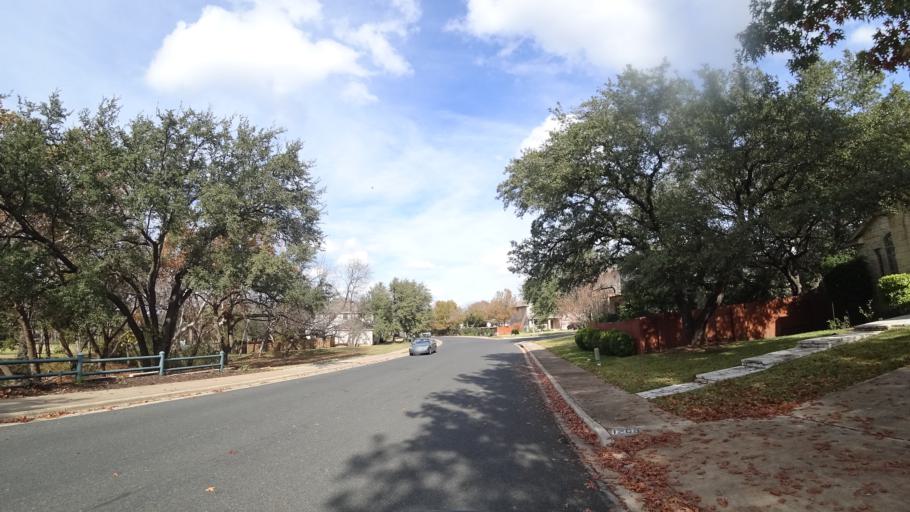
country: US
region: Texas
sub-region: Williamson County
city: Brushy Creek
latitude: 30.5140
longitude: -97.7417
